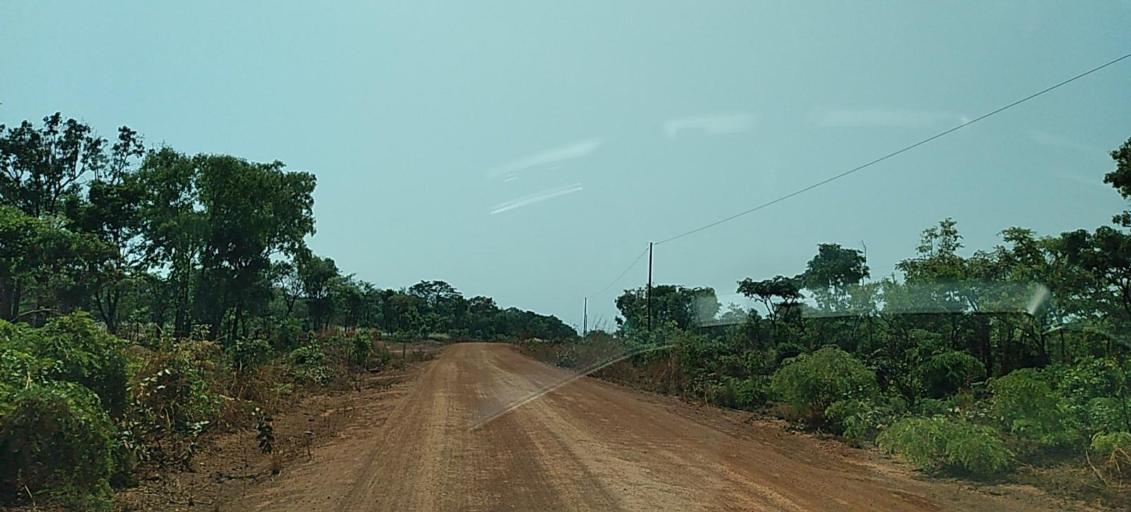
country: ZM
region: North-Western
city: Kansanshi
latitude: -11.9941
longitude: 26.6449
